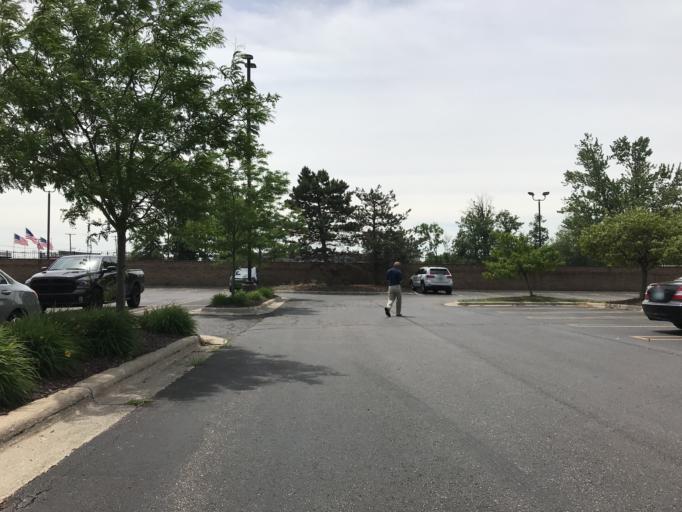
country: US
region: Michigan
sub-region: Oakland County
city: Bingham Farms
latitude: 42.4990
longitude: -83.2891
